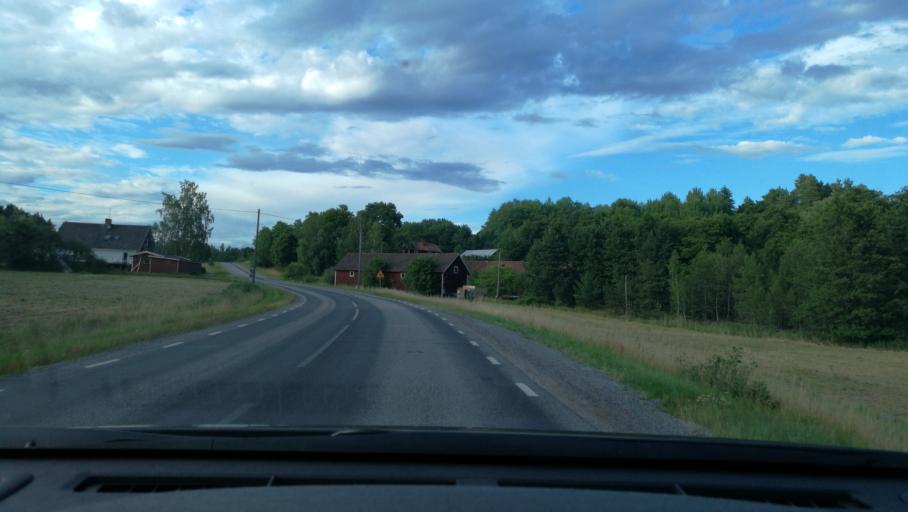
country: SE
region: OEstergoetland
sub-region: Norrkopings Kommun
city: Svartinge
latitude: 58.6911
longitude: 15.9262
